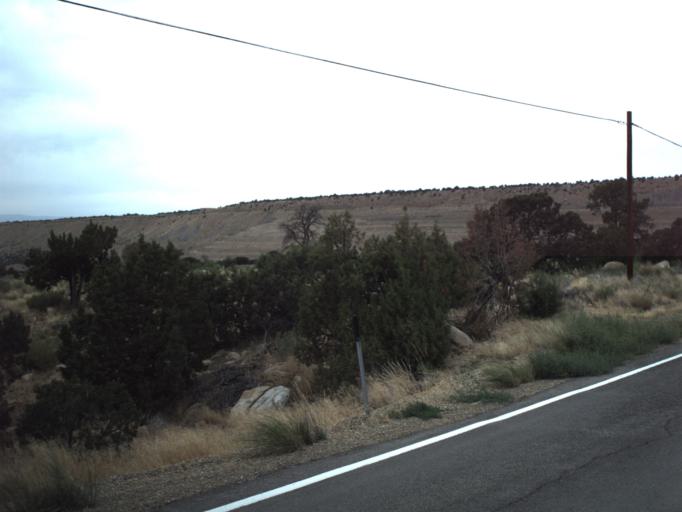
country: US
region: Utah
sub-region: Carbon County
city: East Carbon City
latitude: 39.5334
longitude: -110.4029
